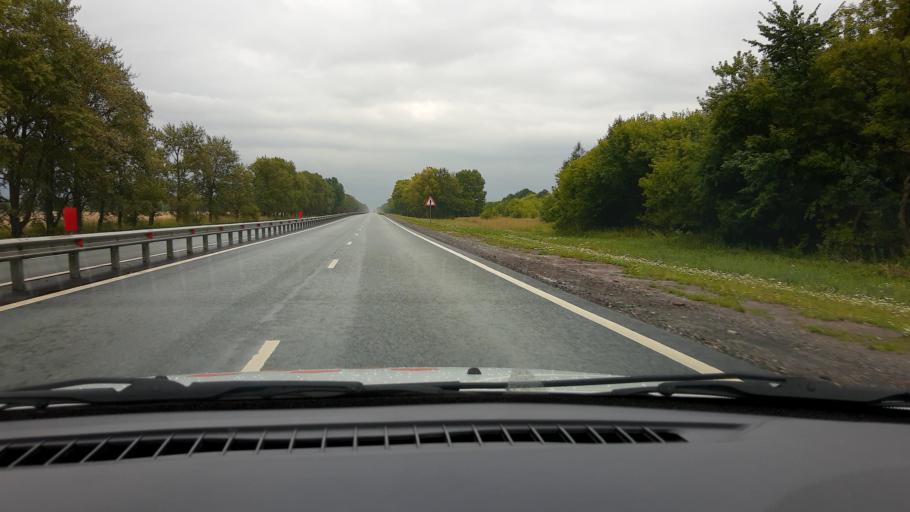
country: RU
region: Chuvashia
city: Yantikovo
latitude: 55.7896
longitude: 47.7519
